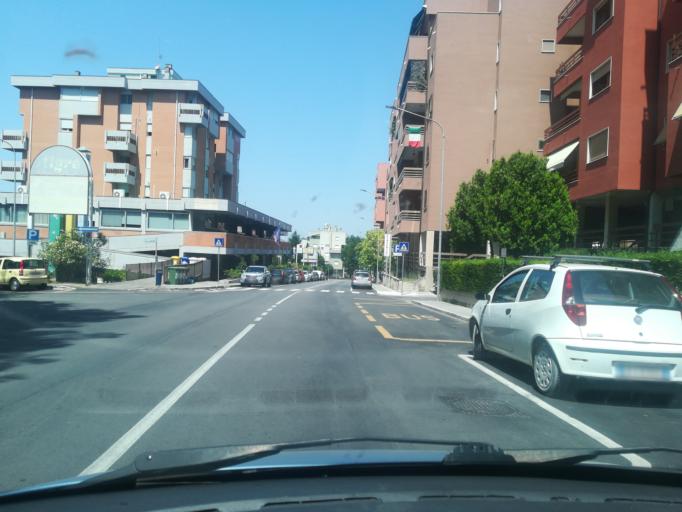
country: IT
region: The Marches
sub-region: Provincia di Macerata
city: Villa Potenza
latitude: 43.2980
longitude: 13.4275
